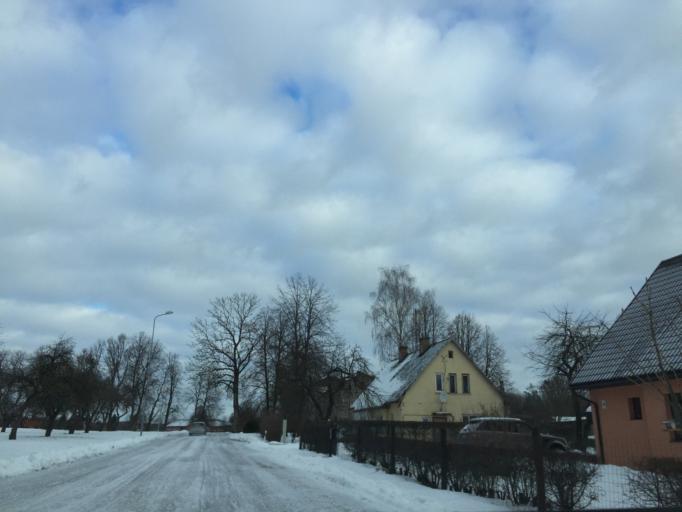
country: LV
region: Lielvarde
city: Lielvarde
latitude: 56.6299
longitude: 24.7502
